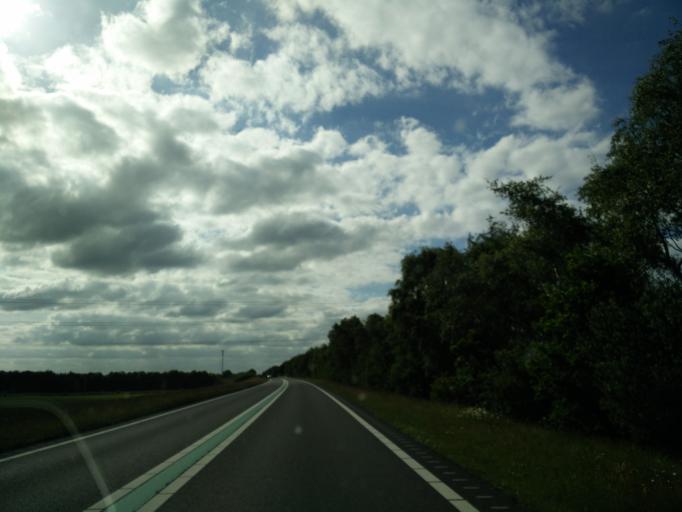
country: NL
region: Drenthe
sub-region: Gemeente Assen
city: Assen
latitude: 52.8720
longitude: 6.5333
